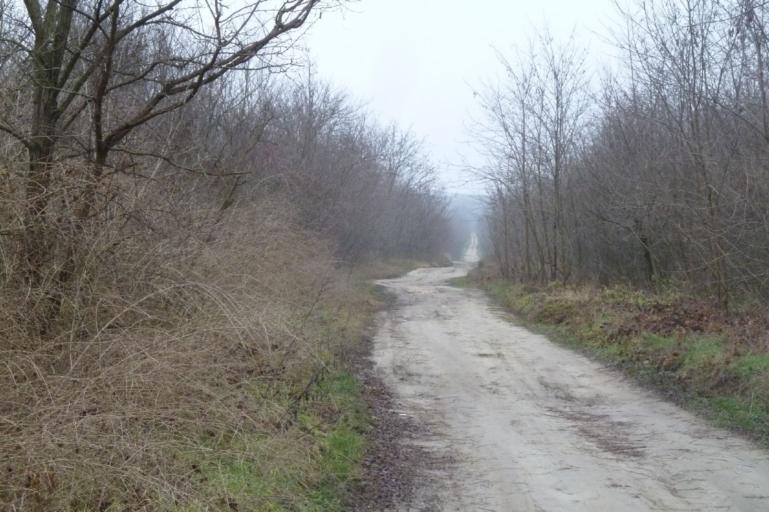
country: HU
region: Pest
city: Pilis
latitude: 47.2952
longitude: 19.5708
